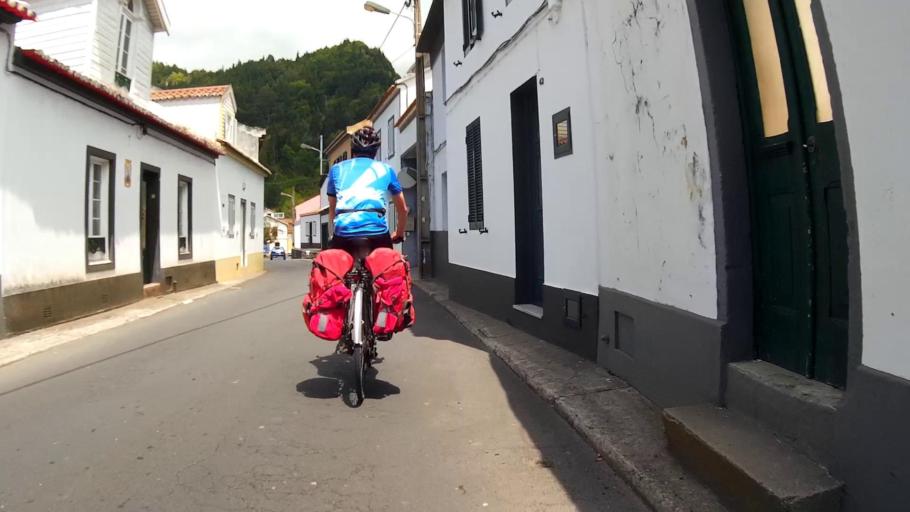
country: PT
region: Azores
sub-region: Povoacao
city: Furnas
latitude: 37.7755
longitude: -25.3121
